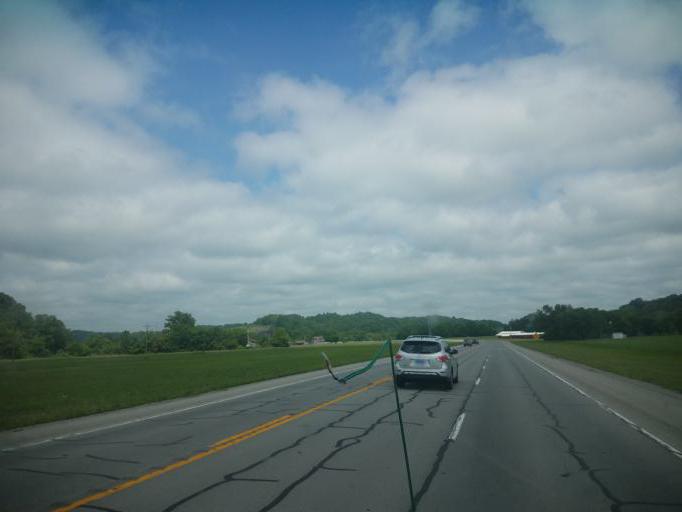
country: US
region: Kentucky
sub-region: Metcalfe County
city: Edmonton
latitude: 36.8428
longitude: -85.5345
